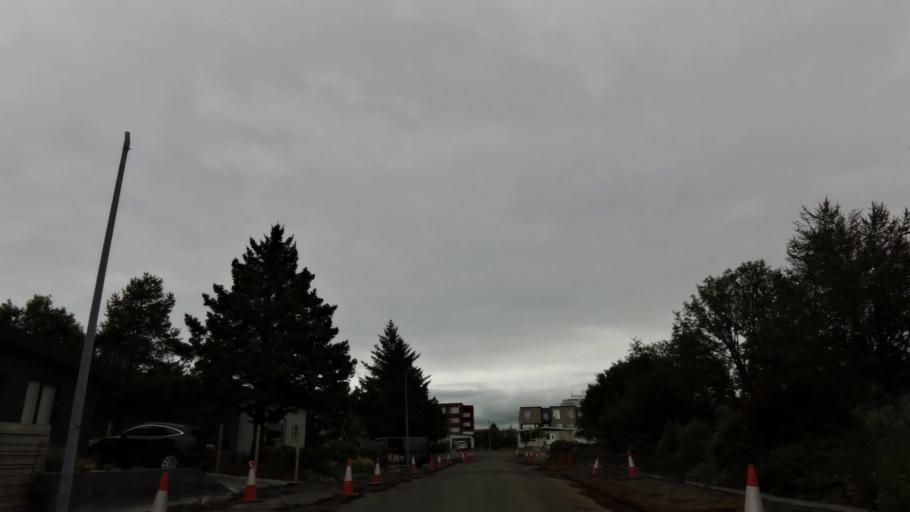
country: IS
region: Capital Region
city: Gardabaer
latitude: 64.0871
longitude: -21.9232
